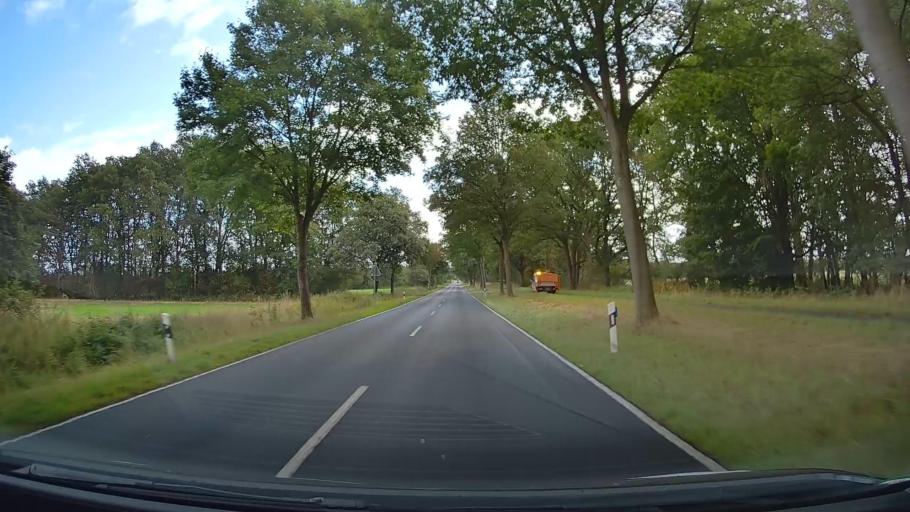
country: DE
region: Lower Saxony
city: Rhade
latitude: 53.3454
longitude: 9.0816
